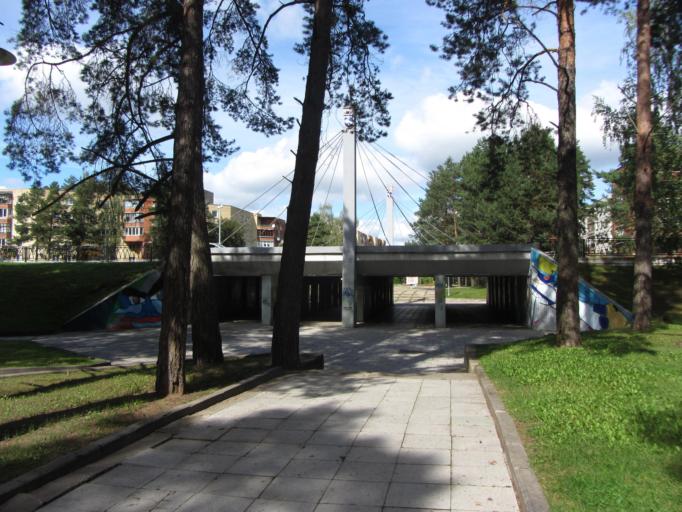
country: LT
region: Utenos apskritis
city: Visaginas
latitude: 55.5964
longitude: 26.4302
